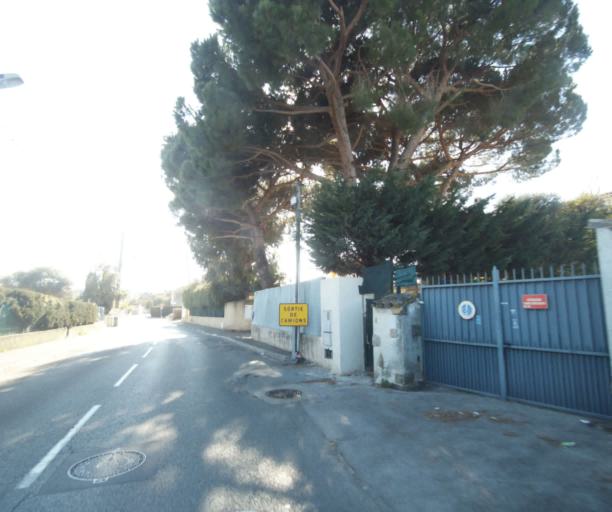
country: FR
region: Provence-Alpes-Cote d'Azur
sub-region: Departement des Alpes-Maritimes
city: Biot
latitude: 43.6058
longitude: 7.1176
